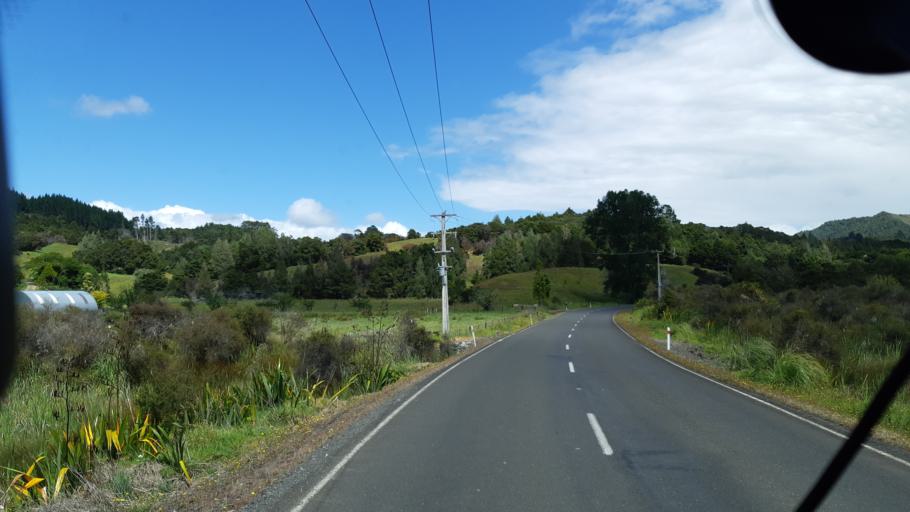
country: NZ
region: Northland
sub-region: Far North District
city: Taipa
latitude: -35.2728
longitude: 173.5101
